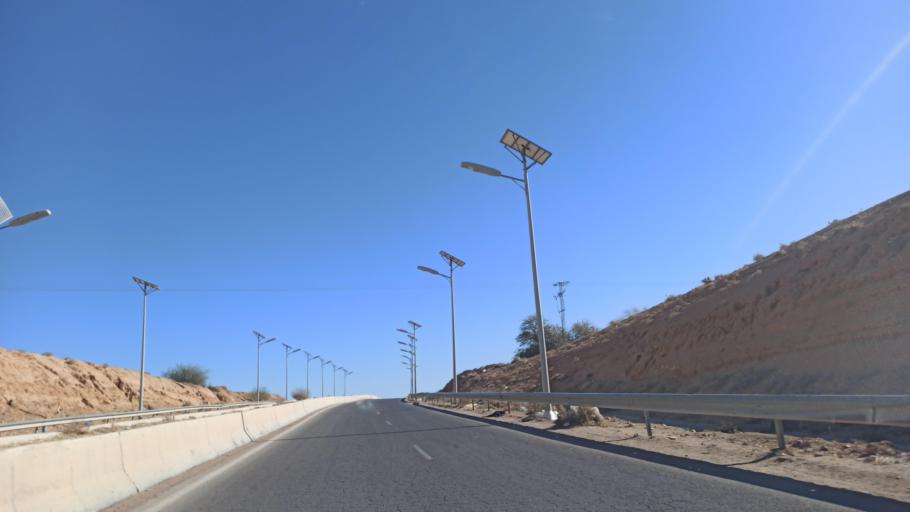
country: TN
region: Gafsa
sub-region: Gafsa Municipality
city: Gafsa
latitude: 34.4331
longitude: 8.8099
